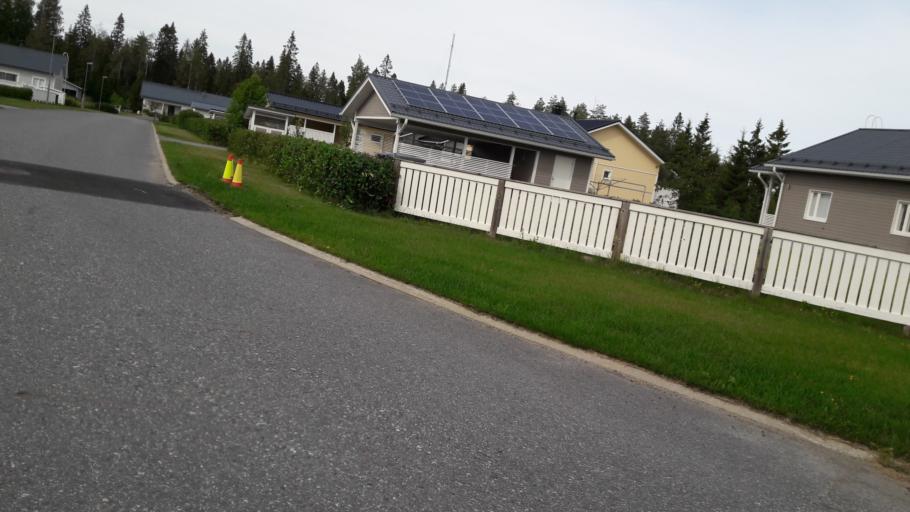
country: FI
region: North Karelia
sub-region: Joensuu
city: Joensuu
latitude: 62.5725
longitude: 29.8252
